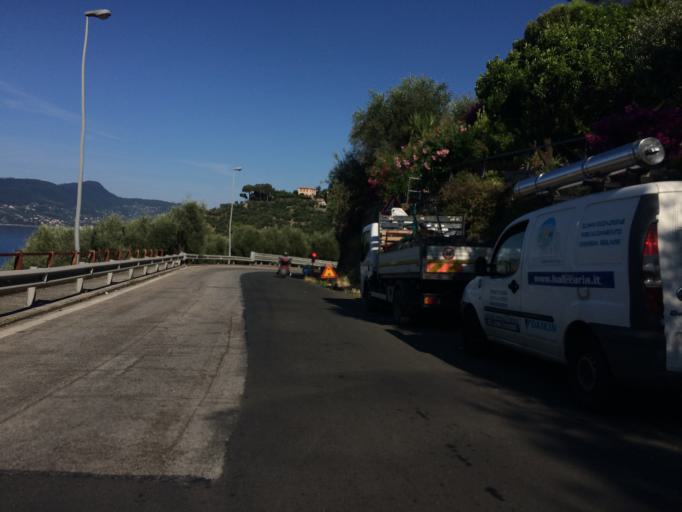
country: IT
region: Liguria
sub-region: Provincia di Genova
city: Zoagli
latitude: 44.3314
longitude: 9.2857
